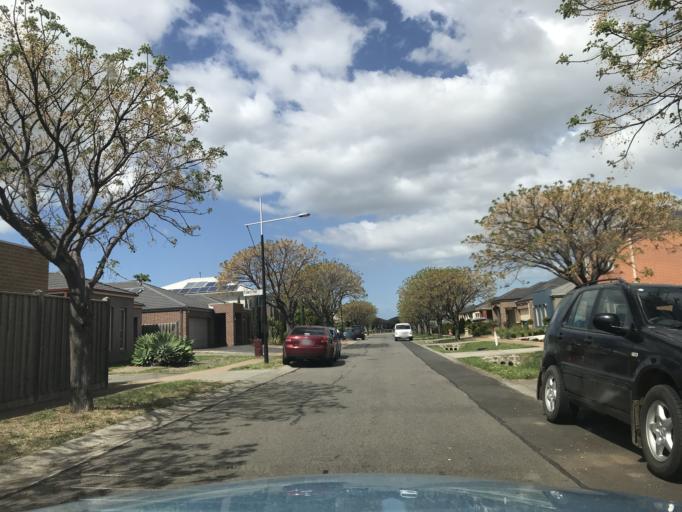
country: AU
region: Victoria
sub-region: Wyndham
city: Williams Landing
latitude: -37.8554
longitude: 144.7341
